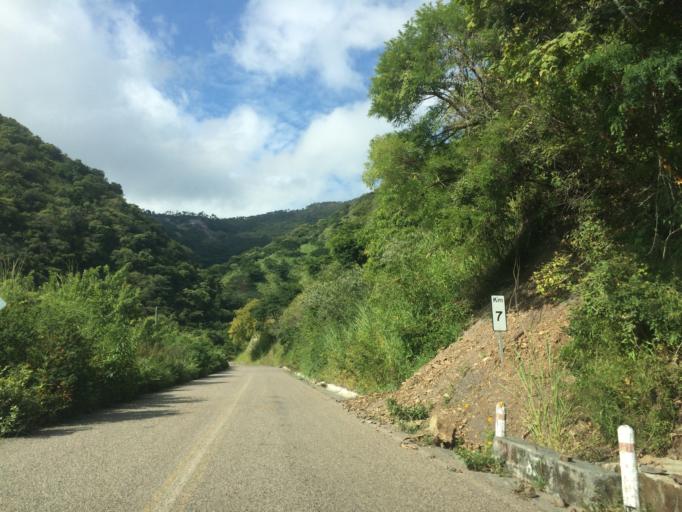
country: MX
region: Nayarit
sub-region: Ahuacatlan
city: Ahuacatlan
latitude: 21.0046
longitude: -104.4821
